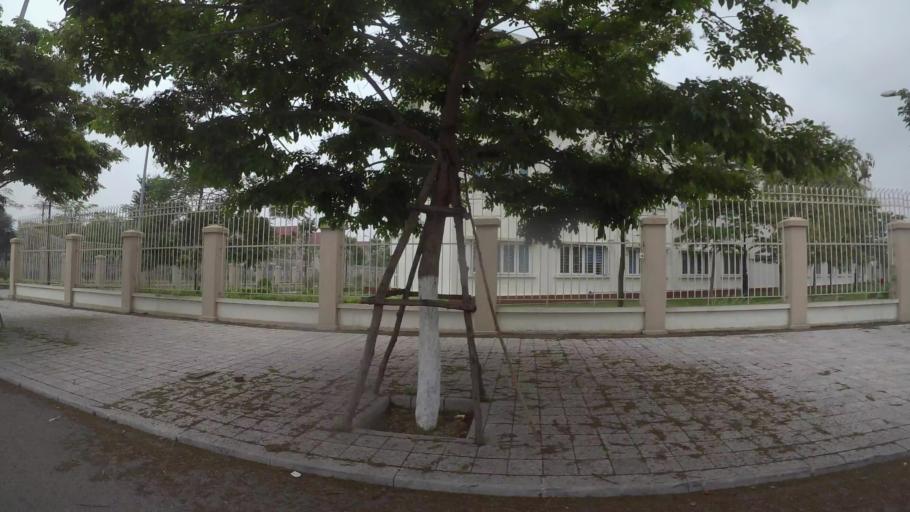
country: VN
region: Ha Noi
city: Ha Dong
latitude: 20.9769
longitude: 105.7533
